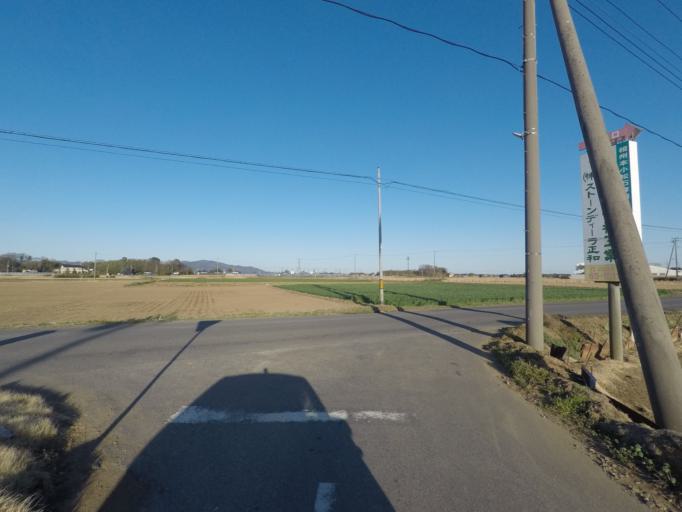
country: JP
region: Ibaraki
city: Ishige
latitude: 36.1341
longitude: 140.0184
